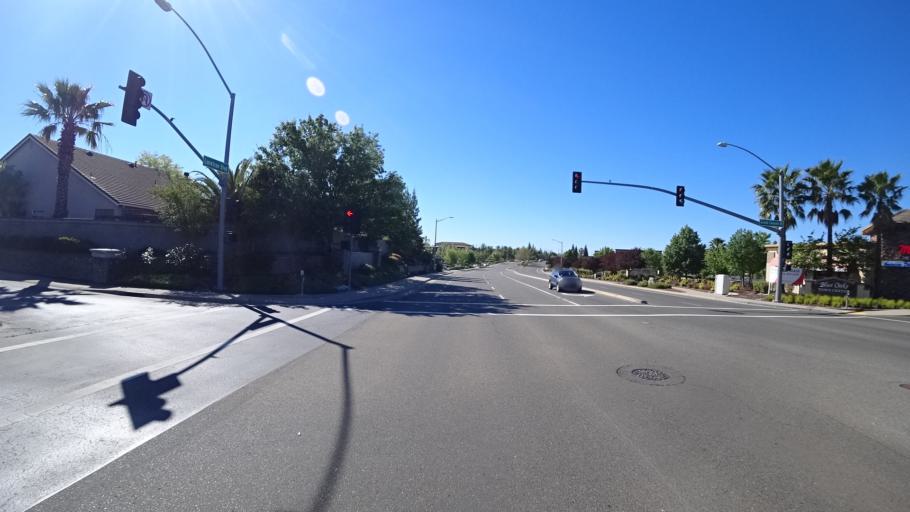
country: US
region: California
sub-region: Placer County
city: Roseville
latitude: 38.7986
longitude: -121.2925
